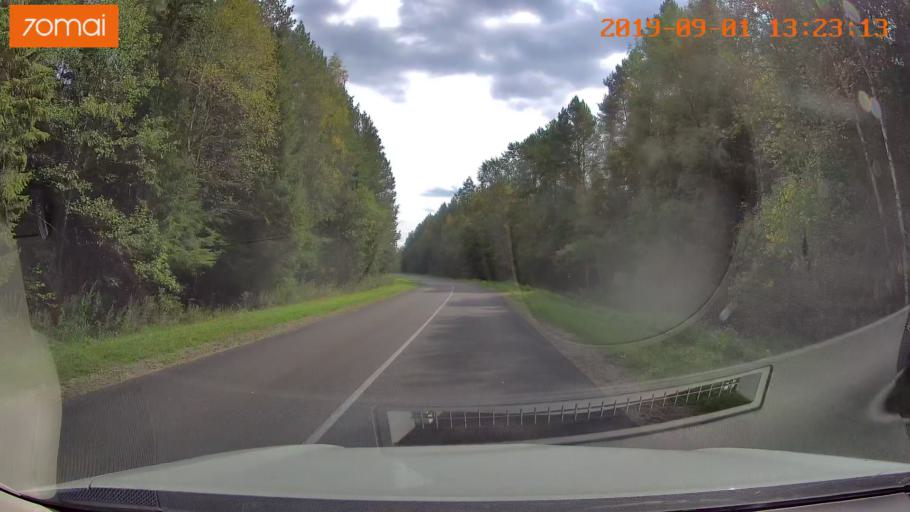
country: RU
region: Kaluga
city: Maloyaroslavets
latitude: 54.8821
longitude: 36.5320
